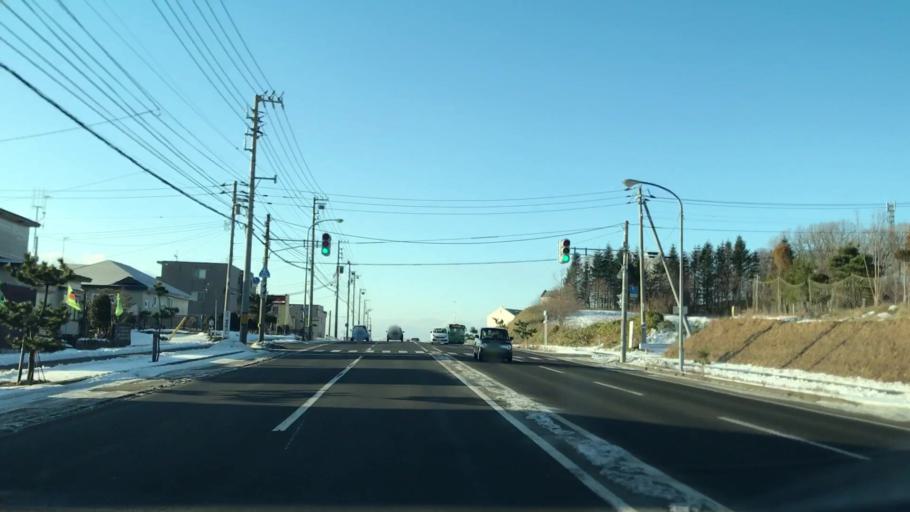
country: JP
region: Hokkaido
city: Muroran
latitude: 42.3893
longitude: 141.0757
